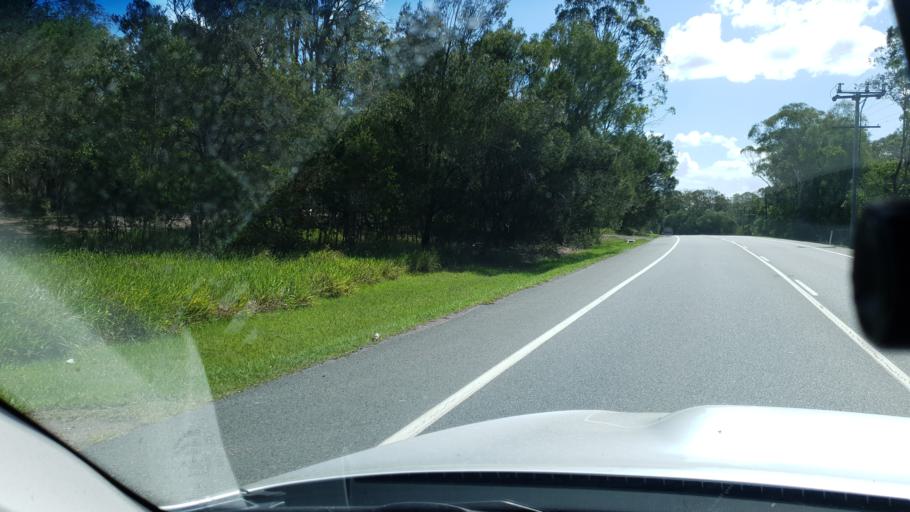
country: AU
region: Queensland
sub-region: Logan
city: Woodridge
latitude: -27.6474
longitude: 153.0885
